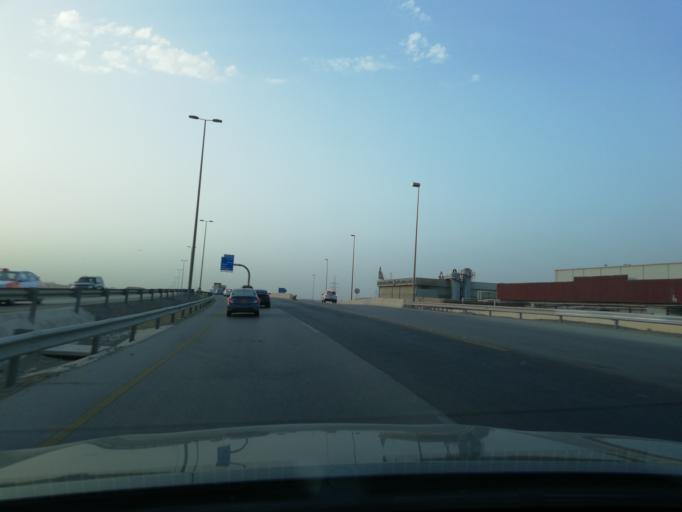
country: OM
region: Muhafazat Masqat
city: As Sib al Jadidah
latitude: 23.5547
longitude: 58.1943
